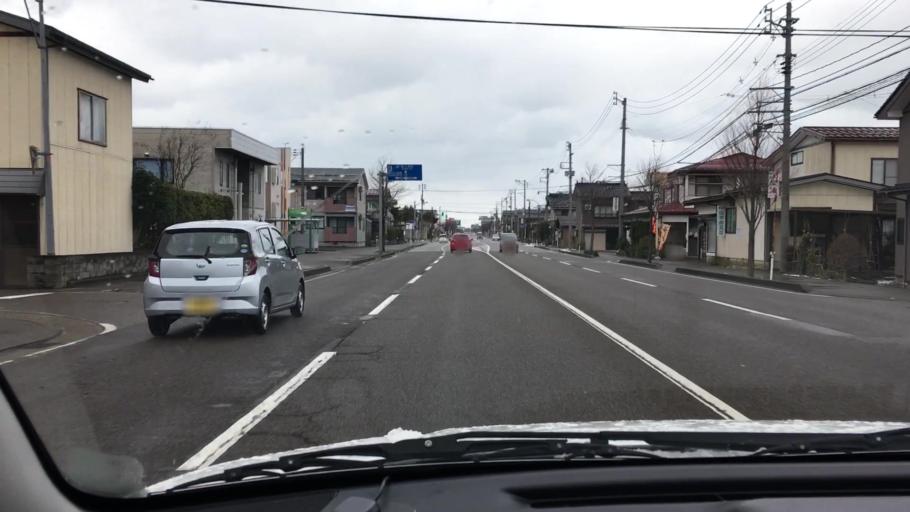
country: JP
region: Niigata
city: Joetsu
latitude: 37.1426
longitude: 138.2286
